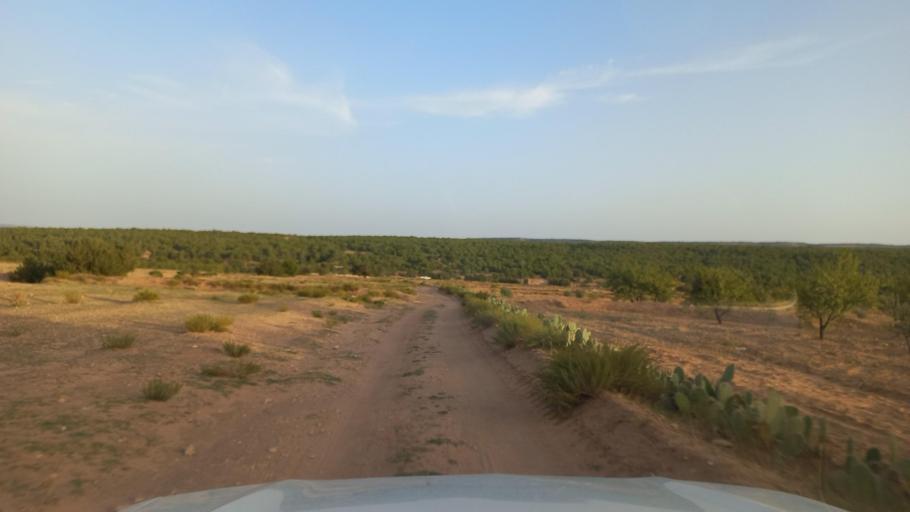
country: TN
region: Al Qasrayn
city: Sbiba
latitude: 35.4111
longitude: 8.9130
